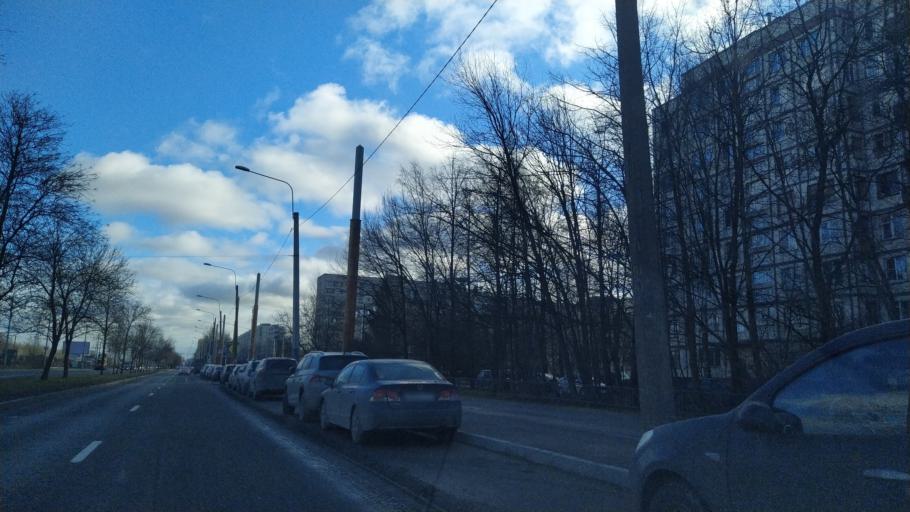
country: RU
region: St.-Petersburg
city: Grazhdanka
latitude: 60.0200
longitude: 30.4139
